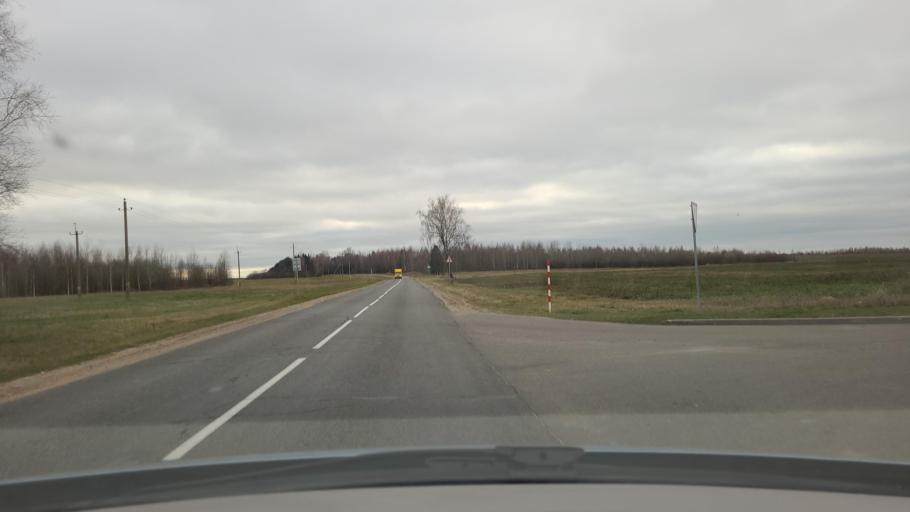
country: BY
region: Minsk
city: Khalopyenichy
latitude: 54.5022
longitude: 28.9568
